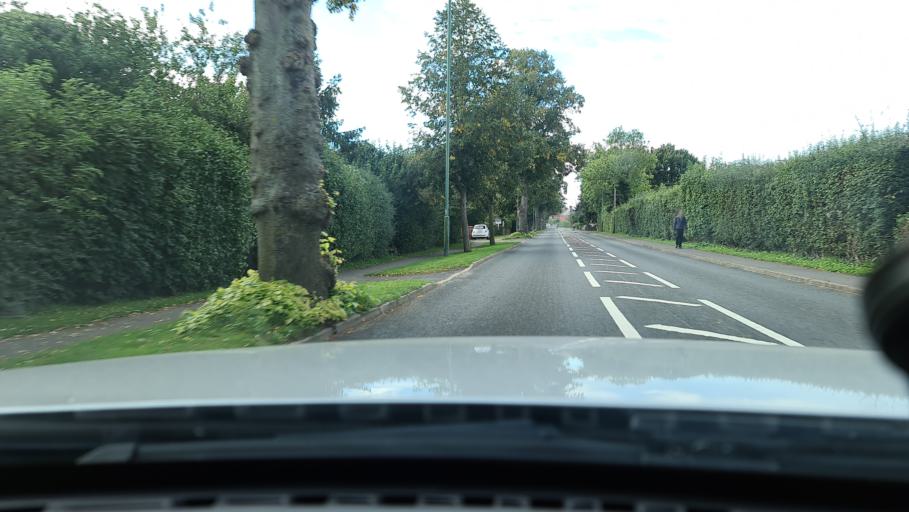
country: GB
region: England
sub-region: Warwickshire
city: Shipston on Stour
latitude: 52.0578
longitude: -1.6238
